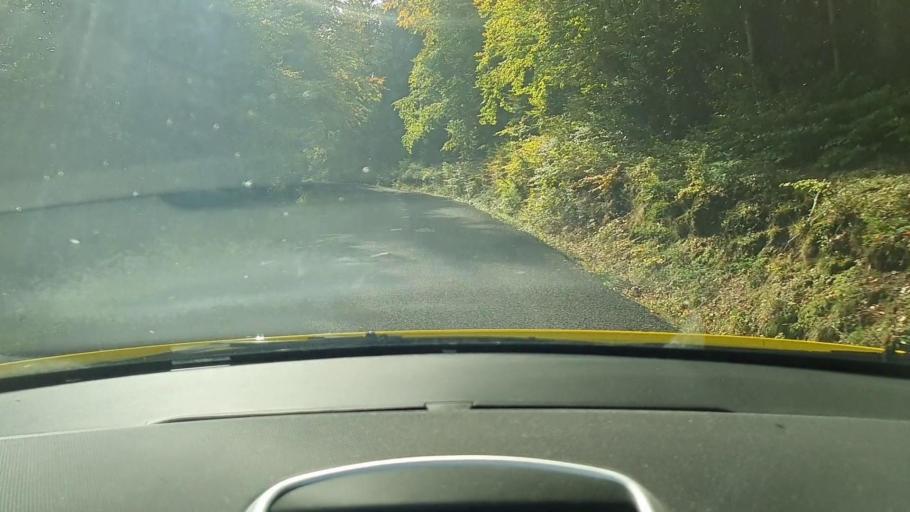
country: FR
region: Languedoc-Roussillon
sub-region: Departement du Gard
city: Valleraugue
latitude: 44.0737
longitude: 3.5672
